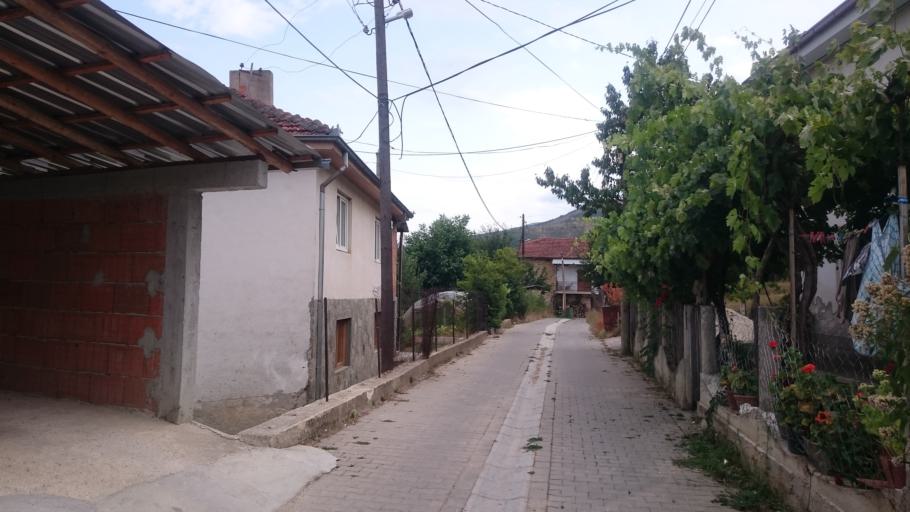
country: MK
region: Makedonski Brod
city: Makedonski Brod
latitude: 41.5165
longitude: 21.2123
